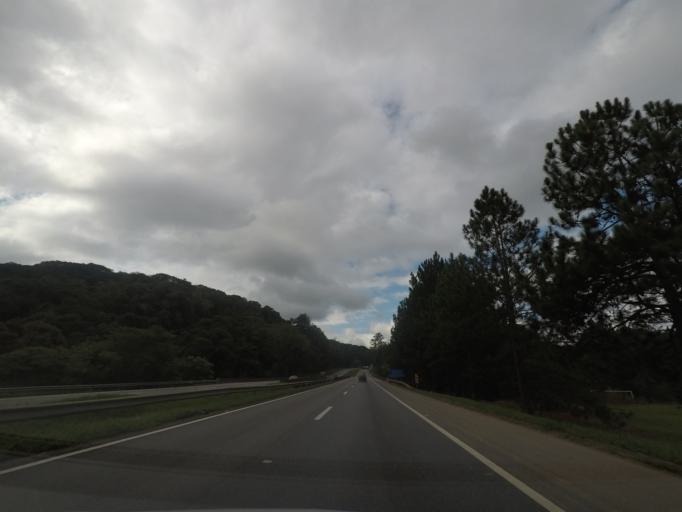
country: BR
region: Sao Paulo
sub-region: Juquitiba
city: Juquitiba
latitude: -23.9410
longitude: -47.0911
